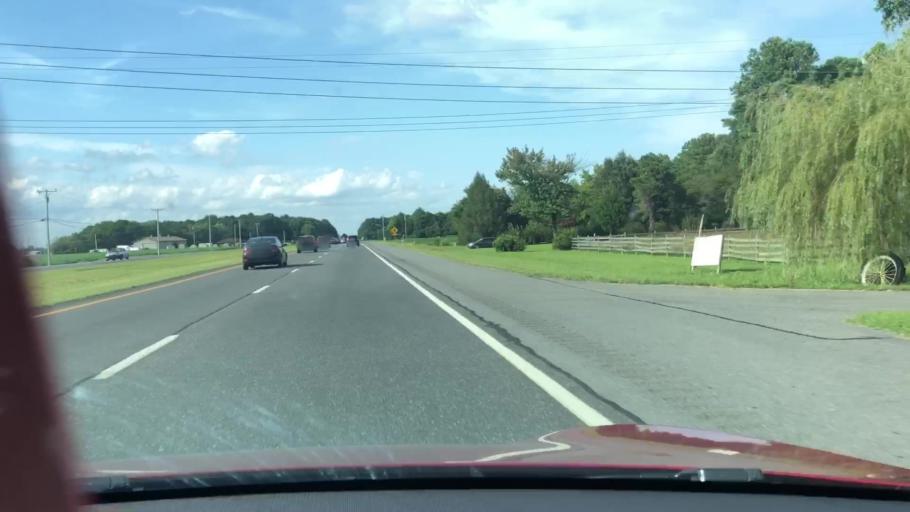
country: US
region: Delaware
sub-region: Kent County
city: Harrington
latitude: 38.8918
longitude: -75.5718
